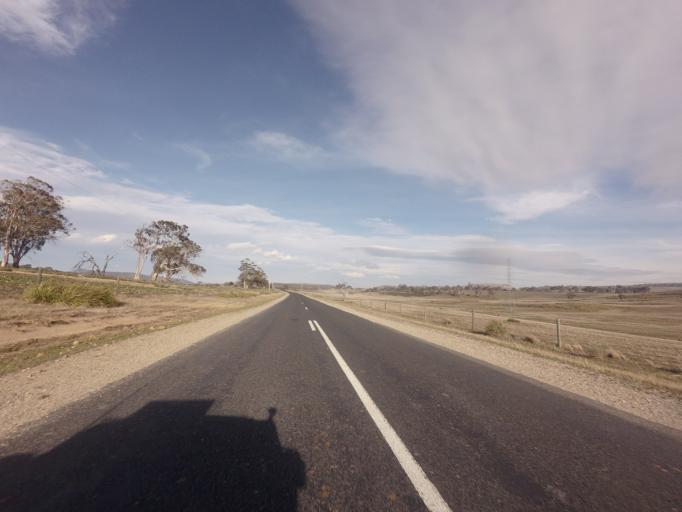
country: AU
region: Tasmania
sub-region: Derwent Valley
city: New Norfolk
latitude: -42.2495
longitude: 146.9275
